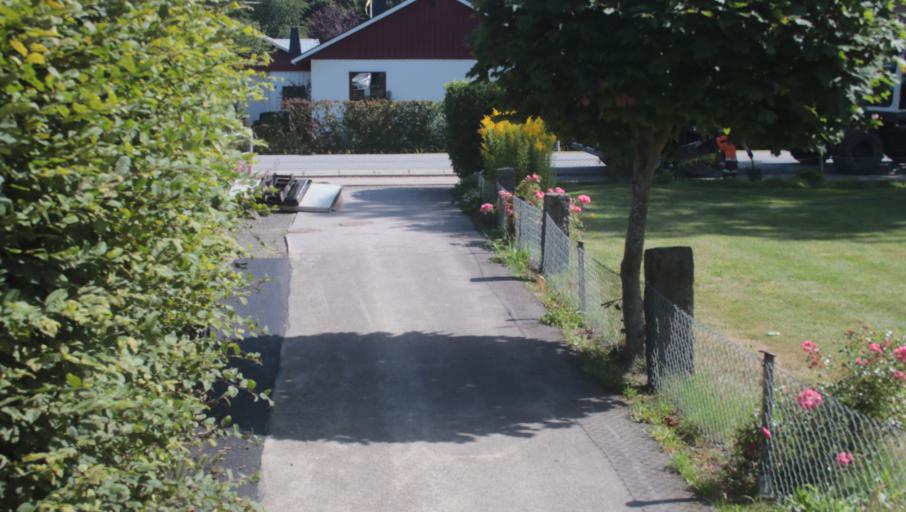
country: SE
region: Blekinge
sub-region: Karlshamns Kommun
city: Karlshamn
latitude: 56.1987
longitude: 14.8252
